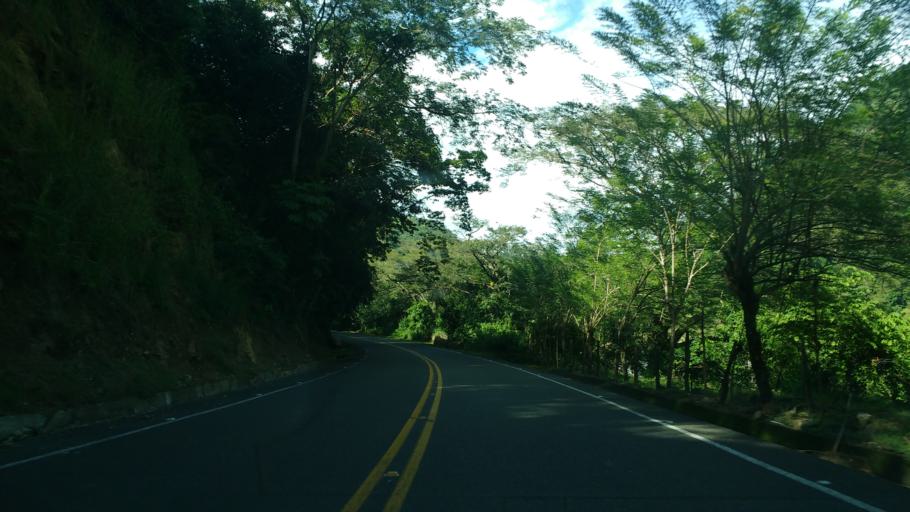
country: CO
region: Antioquia
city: Concordia
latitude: 6.0685
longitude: -75.8609
